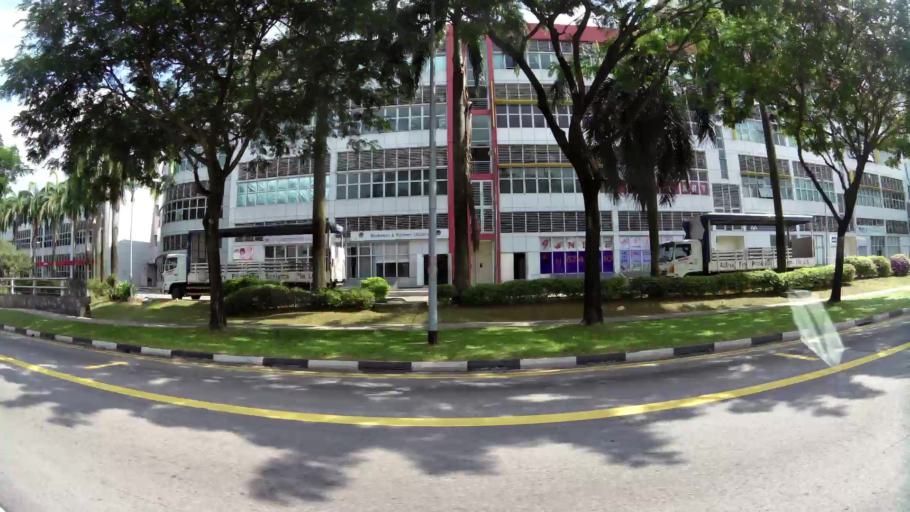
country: SG
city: Singapore
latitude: 1.3339
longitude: 103.9004
